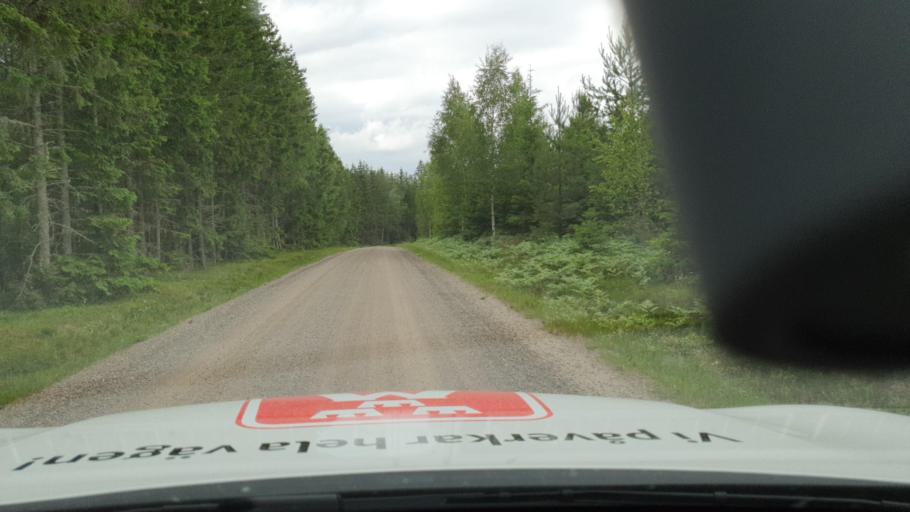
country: SE
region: Vaestra Goetaland
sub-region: Tidaholms Kommun
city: Tidaholm
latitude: 58.1601
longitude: 14.0494
